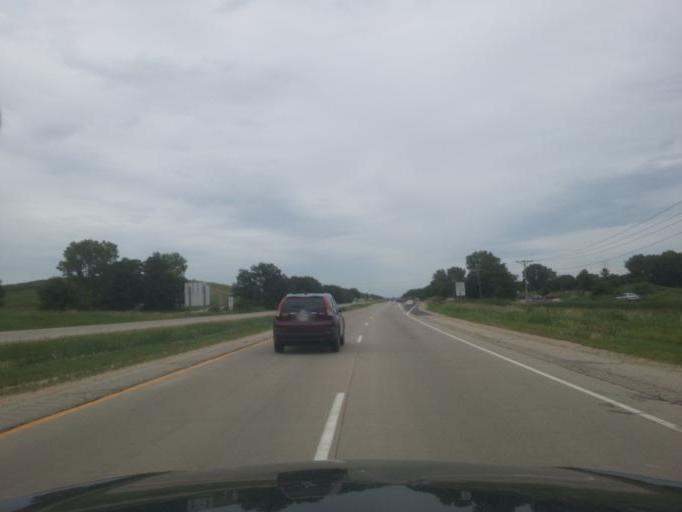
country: US
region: Wisconsin
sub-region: Dane County
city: McFarland
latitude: 43.0449
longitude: -89.2654
